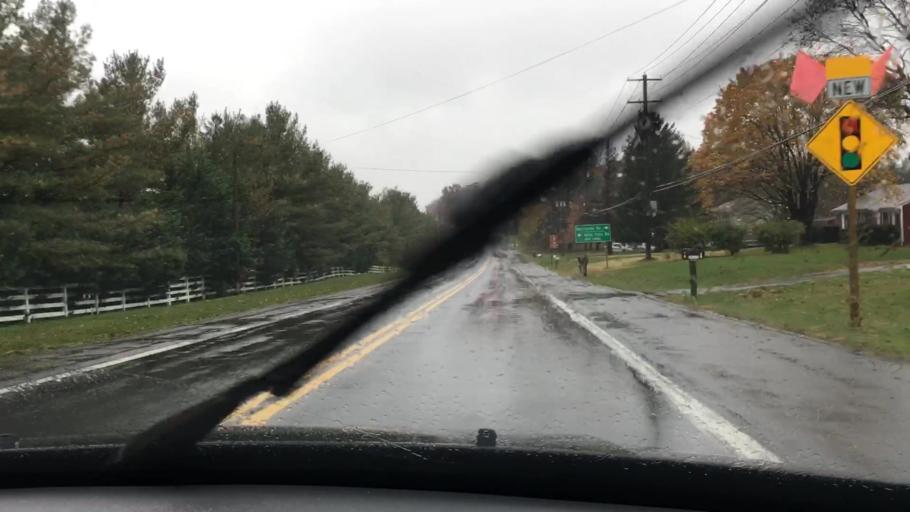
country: US
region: Maryland
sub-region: Carroll County
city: Mount Airy
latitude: 39.4109
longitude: -77.1272
